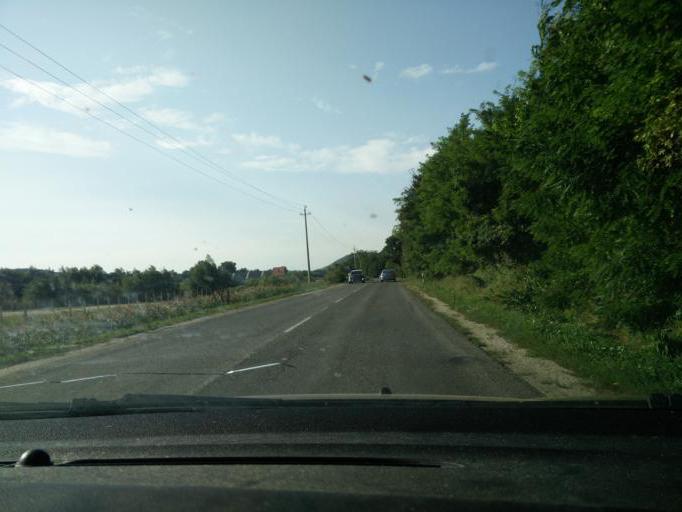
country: HU
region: Pest
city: Piliscsaba
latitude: 47.6388
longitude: 18.8146
